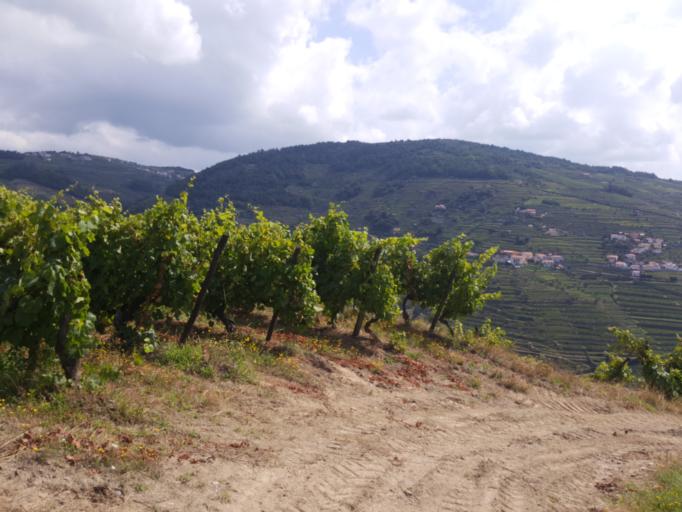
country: PT
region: Vila Real
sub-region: Mesao Frio
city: Mesao Frio
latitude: 41.1749
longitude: -7.8450
